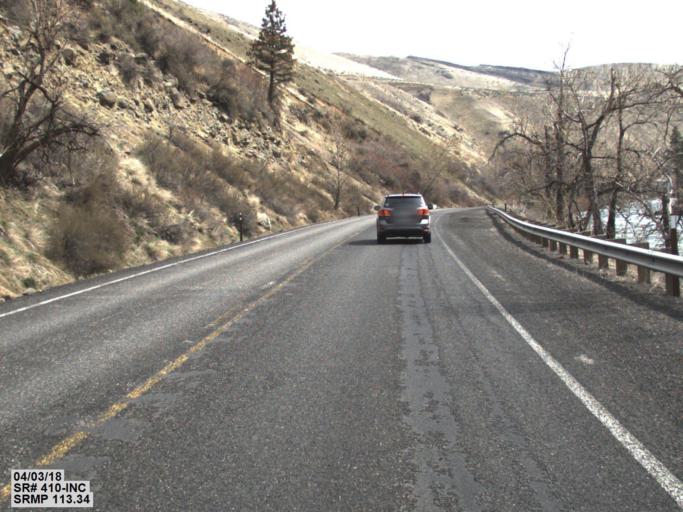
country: US
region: Washington
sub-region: Yakima County
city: Tieton
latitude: 46.7679
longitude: -120.8363
